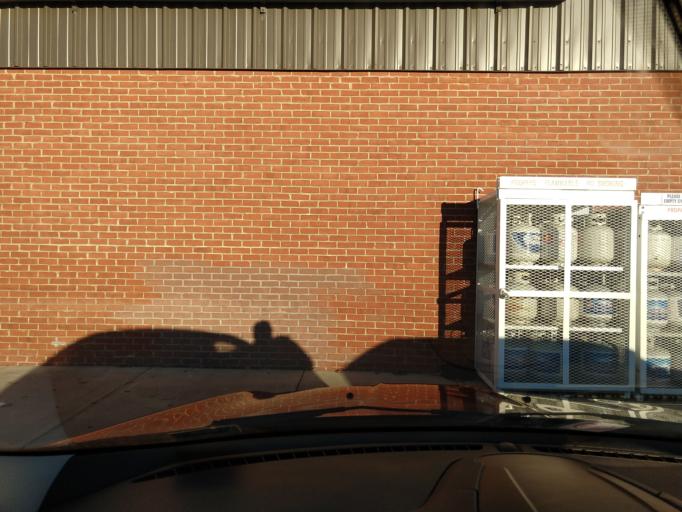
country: US
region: Virginia
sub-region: Franklin County
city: North Shore
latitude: 37.1665
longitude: -79.6359
